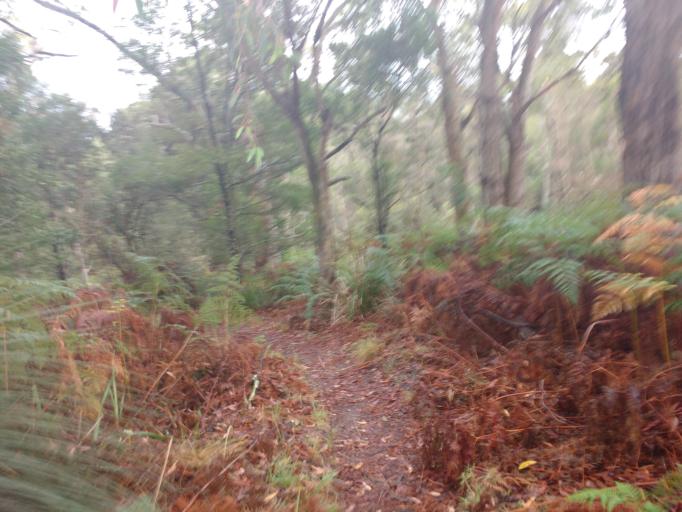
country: AU
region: Victoria
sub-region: Mornington Peninsula
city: Rosebud
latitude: -38.4410
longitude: 144.9321
